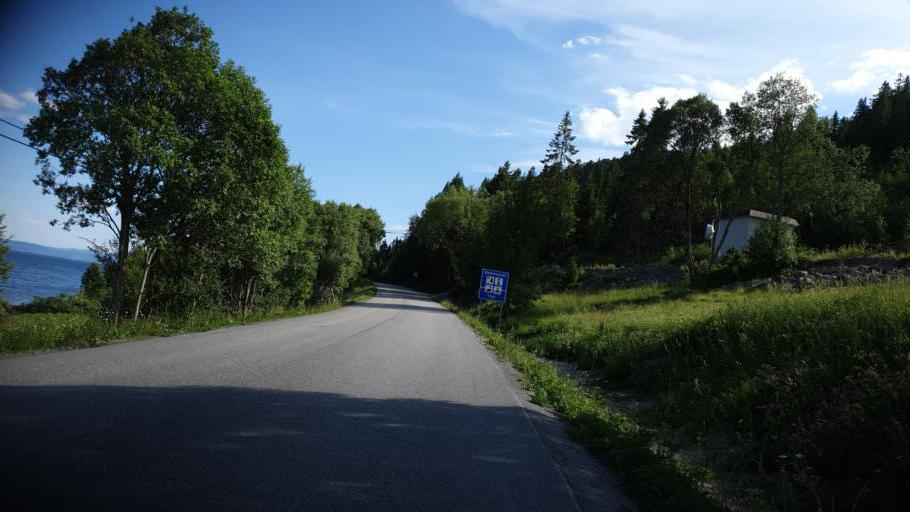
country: NO
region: Sor-Trondelag
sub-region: Trondheim
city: Trondheim
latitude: 63.5803
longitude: 10.4165
